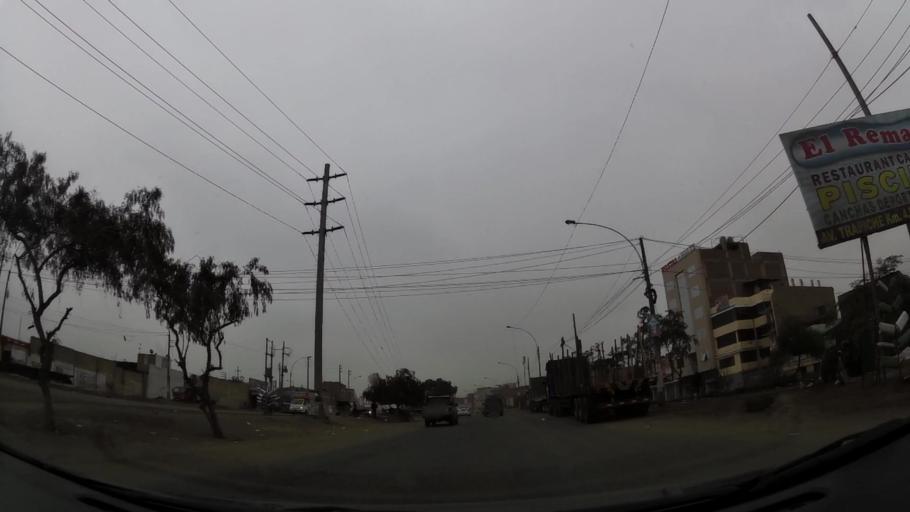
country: PE
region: Lima
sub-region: Lima
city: Independencia
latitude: -11.9305
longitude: -77.0690
